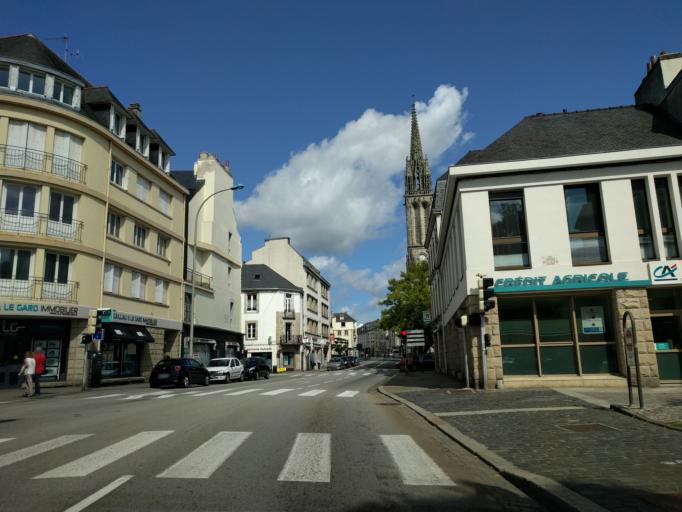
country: FR
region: Brittany
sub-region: Departement du Finistere
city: Quimper
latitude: 47.9950
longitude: -4.1080
